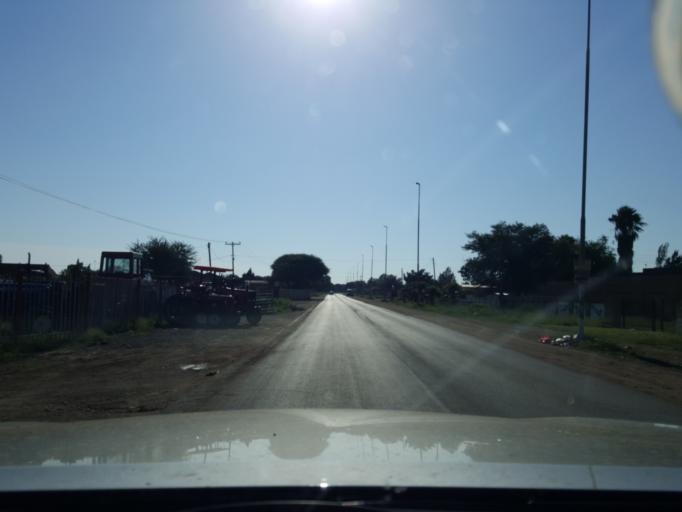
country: ZA
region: North-West
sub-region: Ngaka Modiri Molema District Municipality
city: Mmabatho
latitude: -25.8257
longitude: 25.6361
